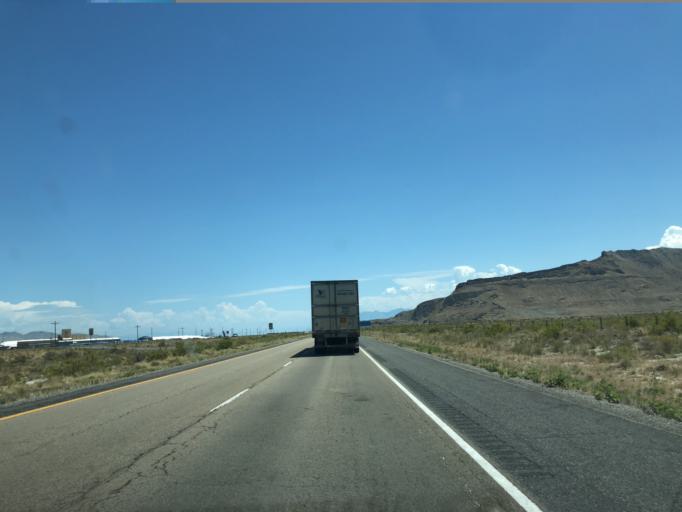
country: US
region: Utah
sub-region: Tooele County
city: Grantsville
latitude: 40.7475
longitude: -112.6713
